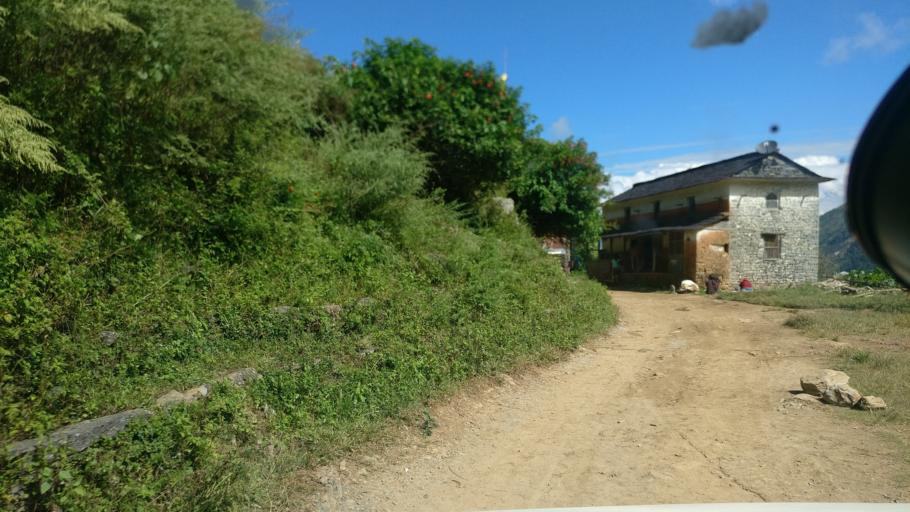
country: NP
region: Western Region
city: Baglung
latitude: 28.1263
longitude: 83.6667
